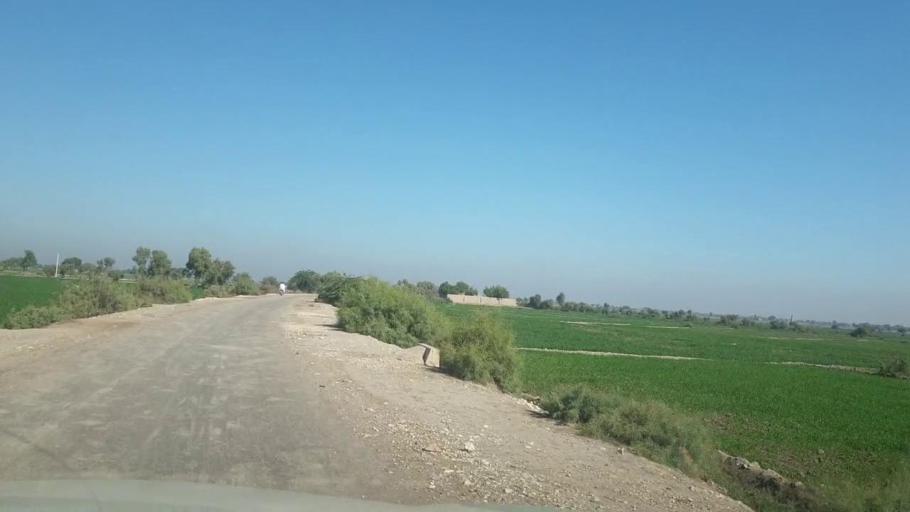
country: PK
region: Sindh
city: Bhan
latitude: 26.5308
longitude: 67.6433
